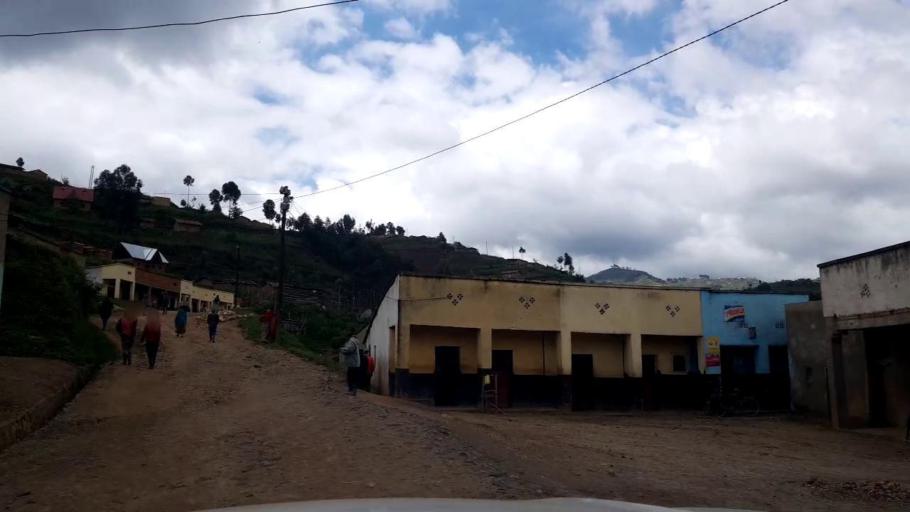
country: RW
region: Western Province
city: Kibuye
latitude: -1.9139
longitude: 29.4573
